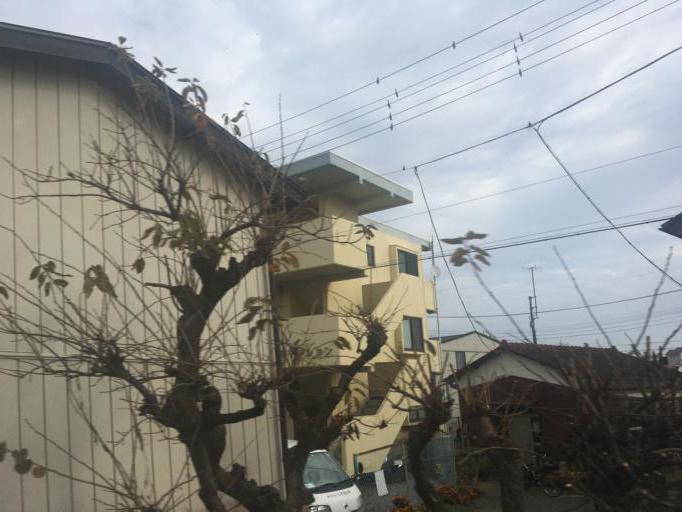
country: JP
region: Tokyo
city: Fussa
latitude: 35.7039
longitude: 139.3602
